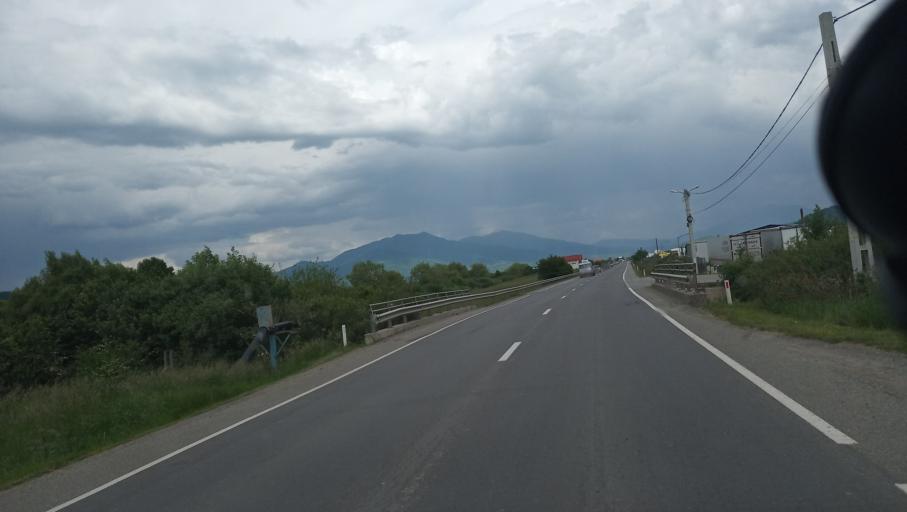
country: RO
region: Bistrita-Nasaud
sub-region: Comuna Livezile
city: Livezile
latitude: 47.1872
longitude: 24.6004
